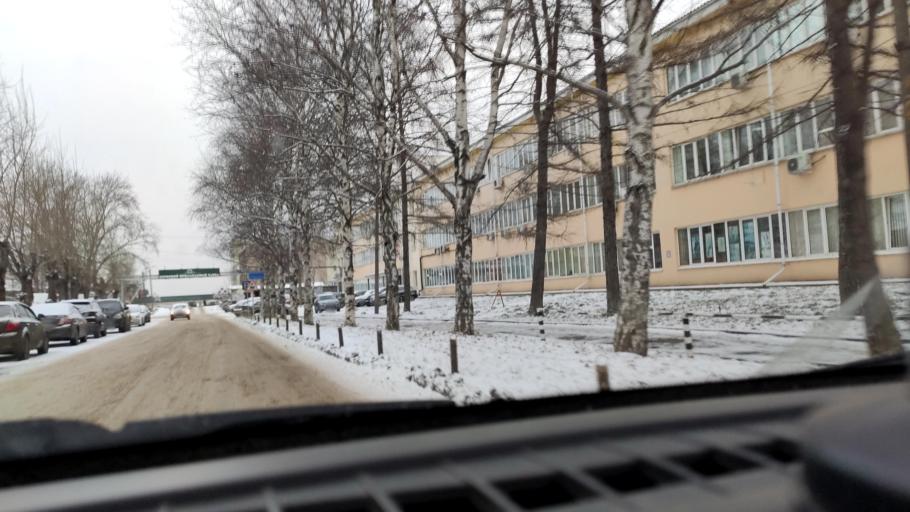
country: RU
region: Perm
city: Perm
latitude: 58.0113
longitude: 56.1821
